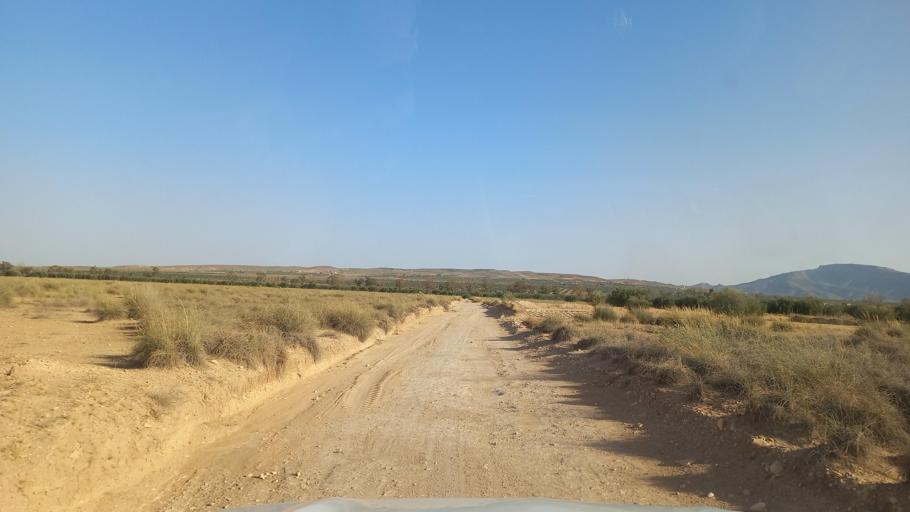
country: TN
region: Al Qasrayn
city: Kasserine
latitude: 35.2298
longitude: 8.9416
